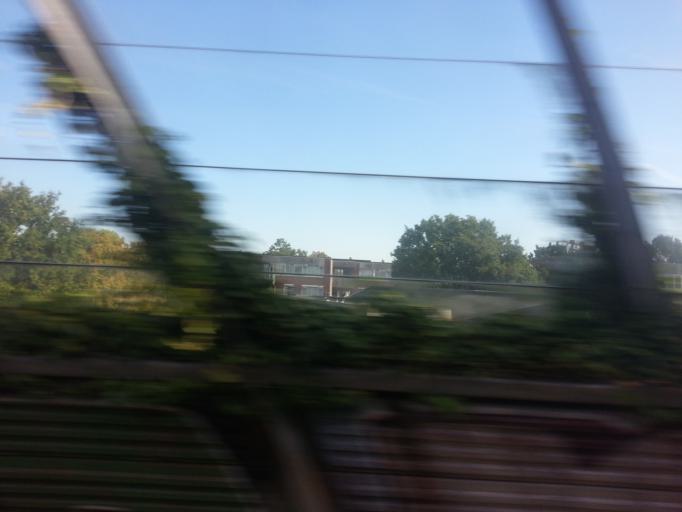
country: NL
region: North Holland
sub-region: Gemeente Amsterdam
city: Amsterdam-Zuidoost
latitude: 52.2998
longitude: 4.9589
